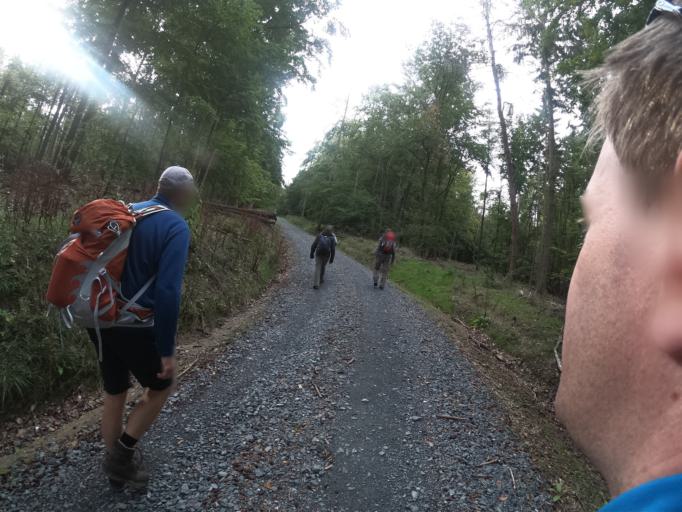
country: DE
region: Hesse
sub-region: Regierungsbezirk Darmstadt
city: Idstein
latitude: 50.2342
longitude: 8.2413
